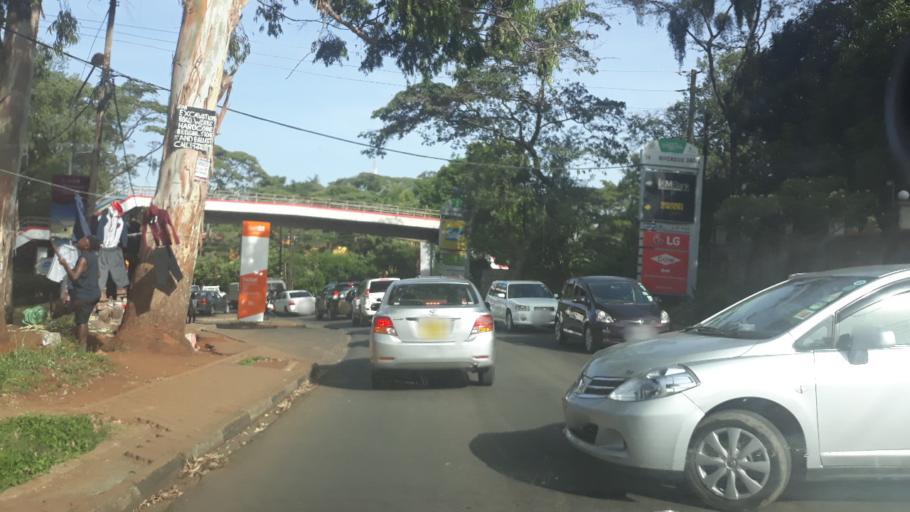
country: KE
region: Nairobi Area
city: Nairobi
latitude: -1.2725
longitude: 36.8033
